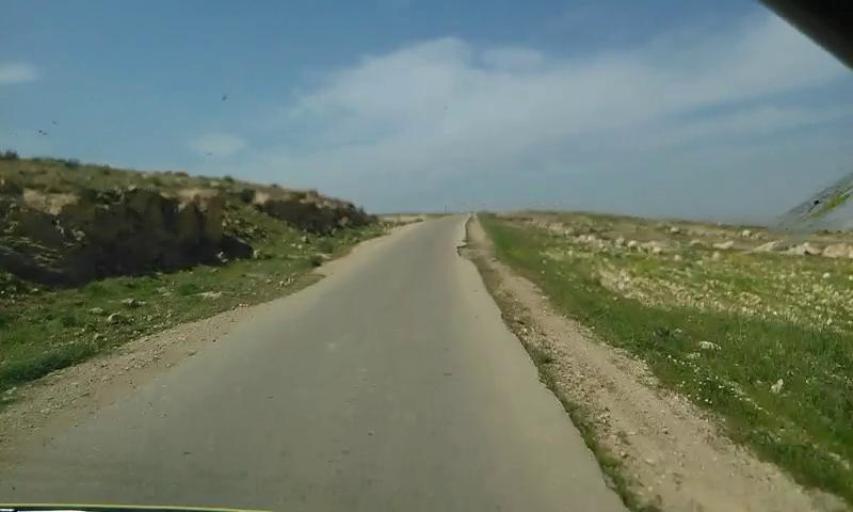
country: PS
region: West Bank
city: Khallat al Mayyah
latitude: 31.4401
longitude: 35.2056
